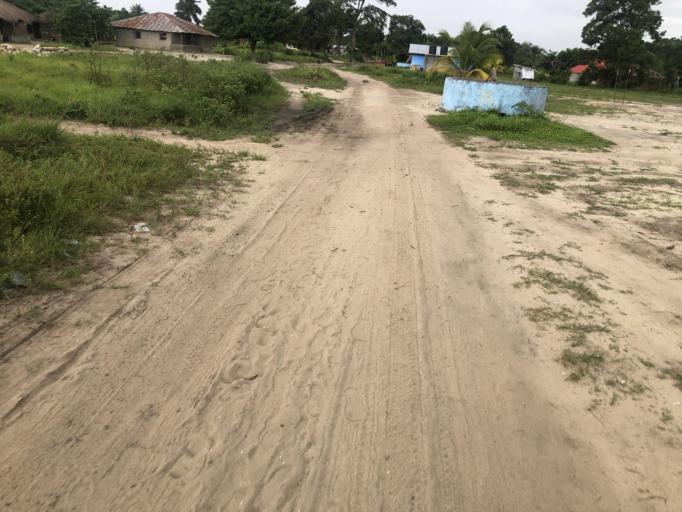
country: SL
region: Southern Province
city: Bonthe
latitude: 7.5243
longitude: -12.5096
